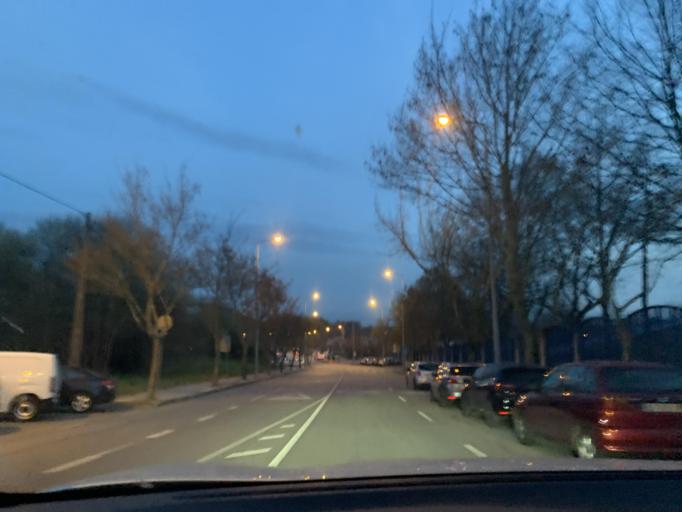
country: PT
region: Viseu
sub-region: Viseu
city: Viseu
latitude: 40.6510
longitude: -7.9041
